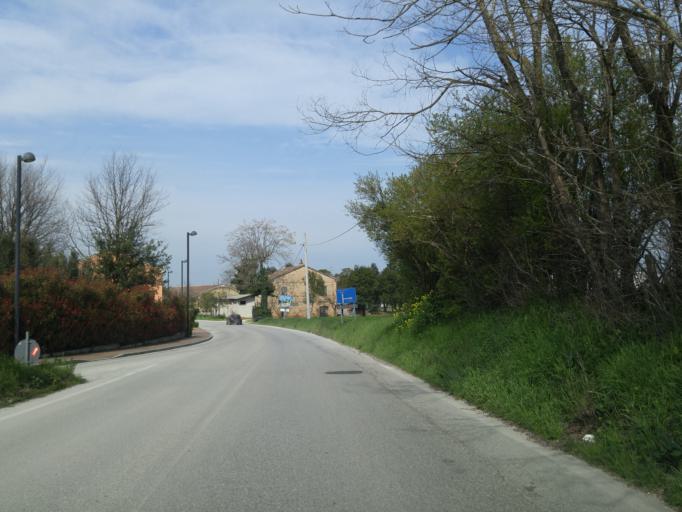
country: IT
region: The Marches
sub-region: Provincia di Pesaro e Urbino
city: Villanova
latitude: 43.7357
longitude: 12.9369
